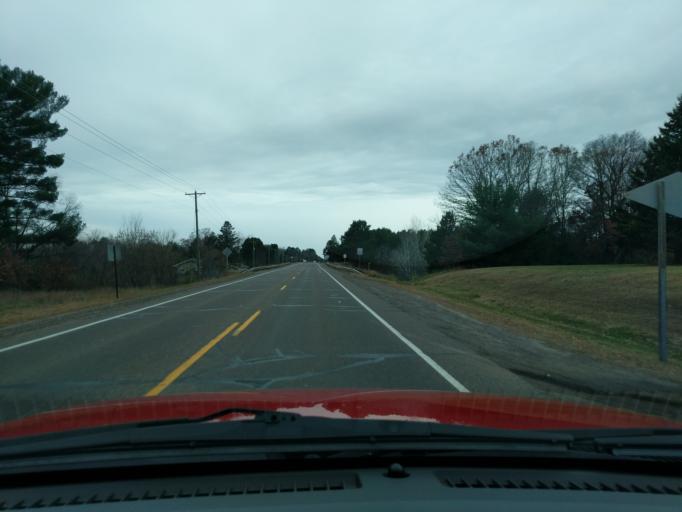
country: US
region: Wisconsin
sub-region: Washburn County
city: Spooner
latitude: 45.8217
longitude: -91.9004
